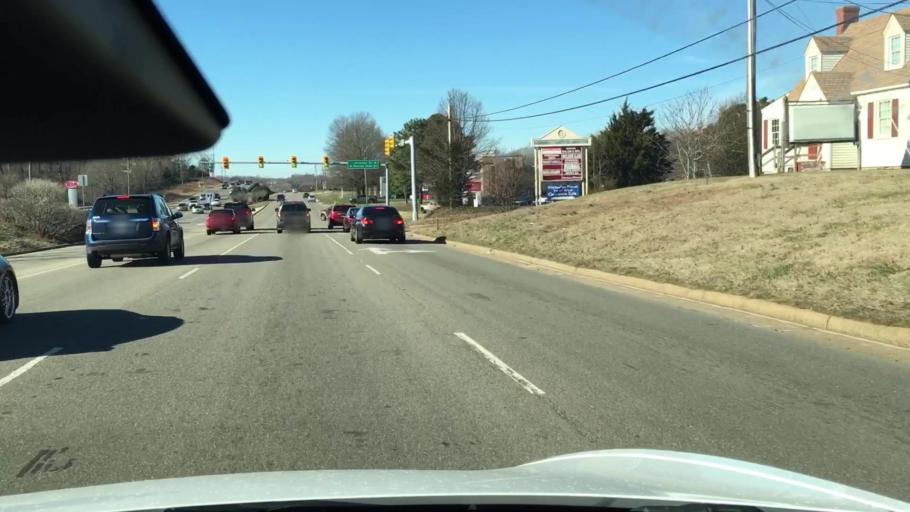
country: US
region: Virginia
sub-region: Chesterfield County
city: Bon Air
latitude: 37.5048
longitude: -77.6170
